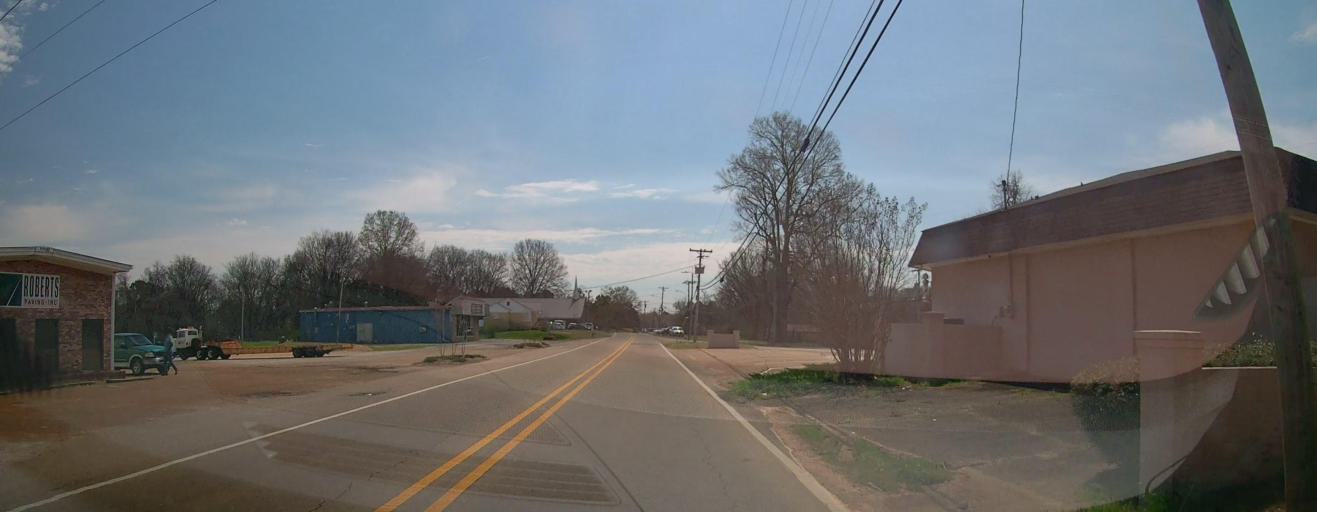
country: US
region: Mississippi
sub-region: Union County
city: New Albany
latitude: 34.4878
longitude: -89.0025
